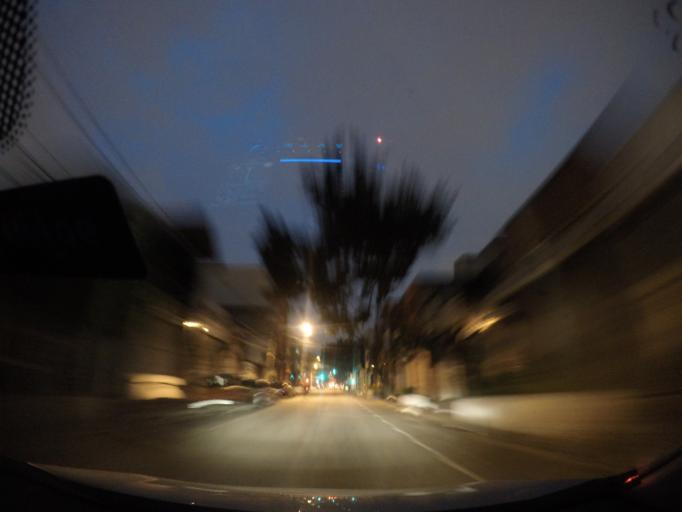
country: BR
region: Sao Paulo
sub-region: Sao Paulo
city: Sao Paulo
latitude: -23.5368
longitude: -46.6155
